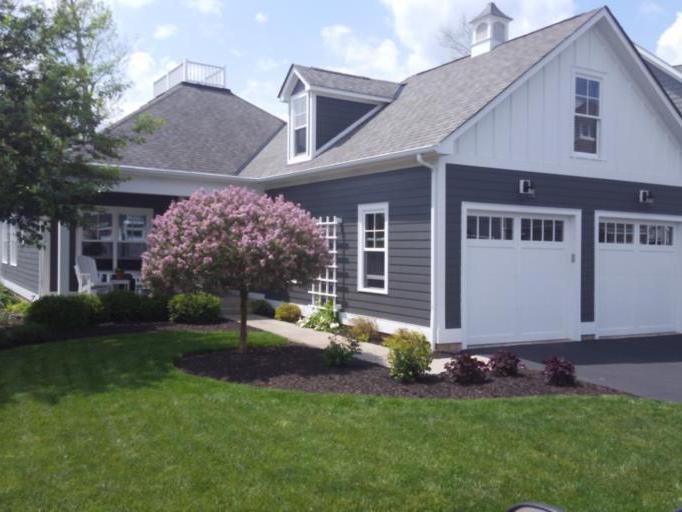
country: US
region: Ohio
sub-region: Perry County
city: Thornport
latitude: 39.9206
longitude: -82.4167
